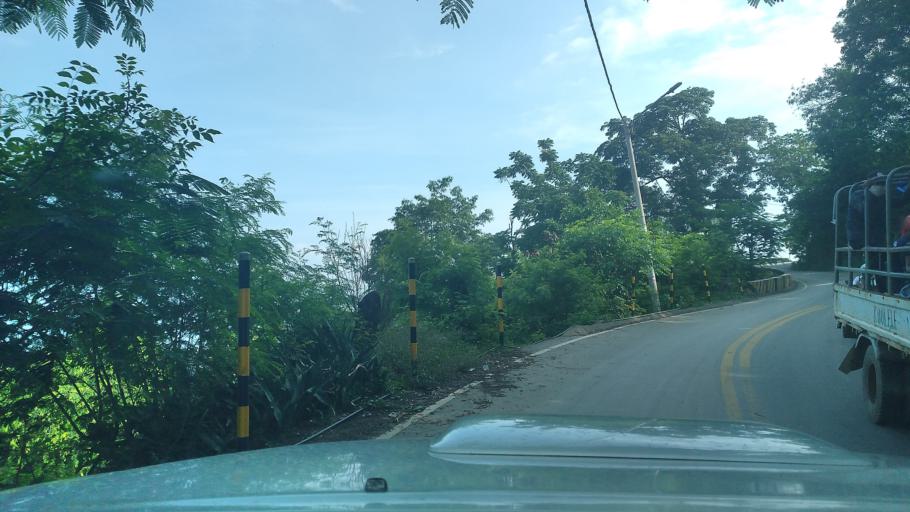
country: TL
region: Dili
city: Dili
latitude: -8.5716
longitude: 125.5862
